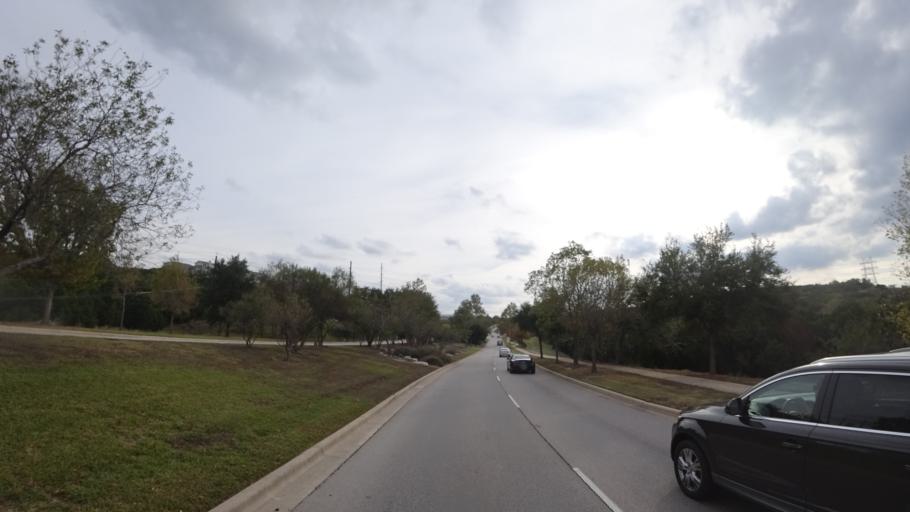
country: US
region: Texas
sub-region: Travis County
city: Hudson Bend
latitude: 30.3868
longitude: -97.8825
